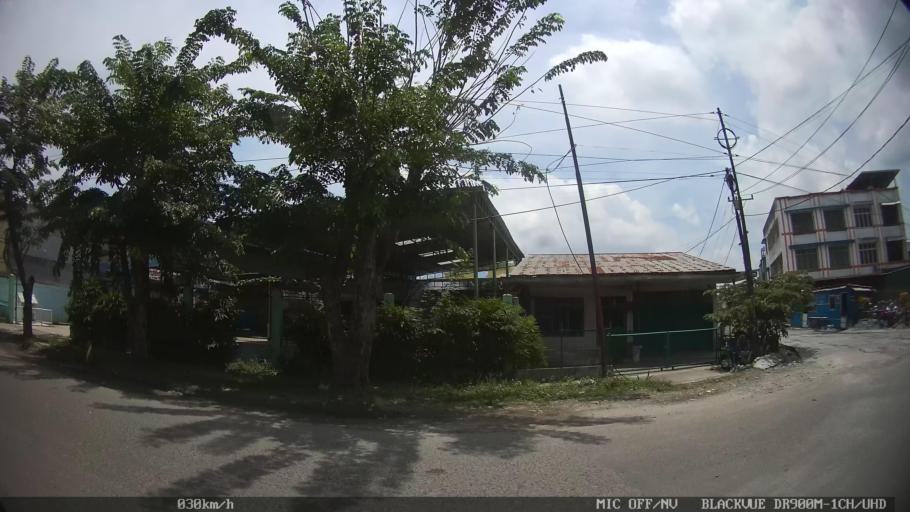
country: ID
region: North Sumatra
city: Labuhan Deli
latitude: 3.7197
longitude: 98.6696
